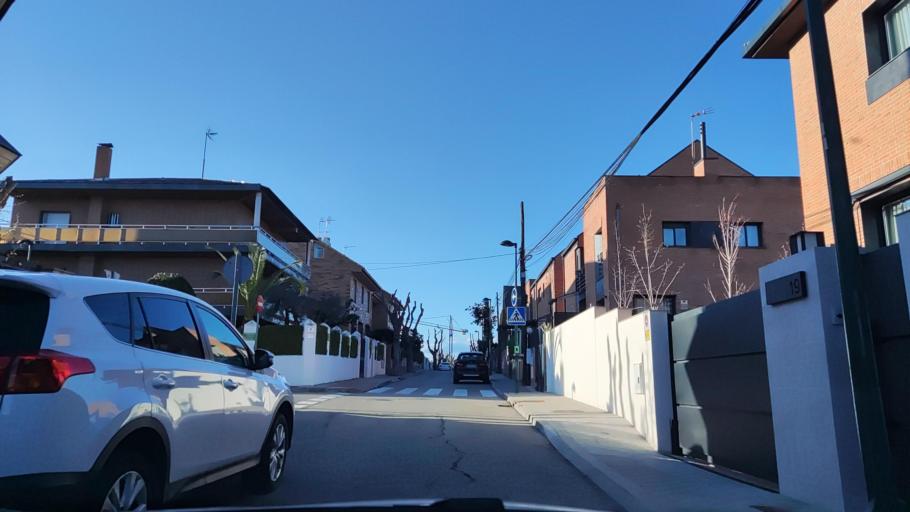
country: ES
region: Madrid
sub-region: Provincia de Madrid
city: Latina
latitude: 40.4075
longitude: -3.7805
